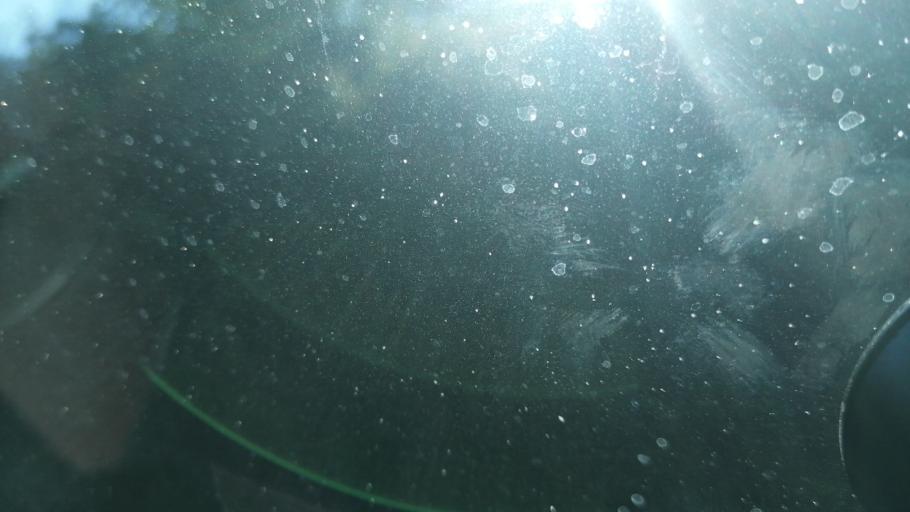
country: PT
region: Porto
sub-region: Santo Tirso
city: Sao Miguel do Couto
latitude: 41.3198
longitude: -8.4693
